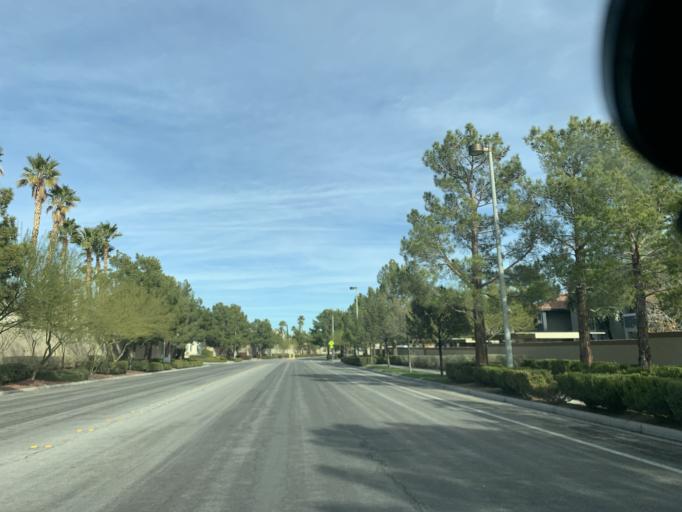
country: US
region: Nevada
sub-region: Clark County
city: Summerlin South
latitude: 36.1488
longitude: -115.3024
